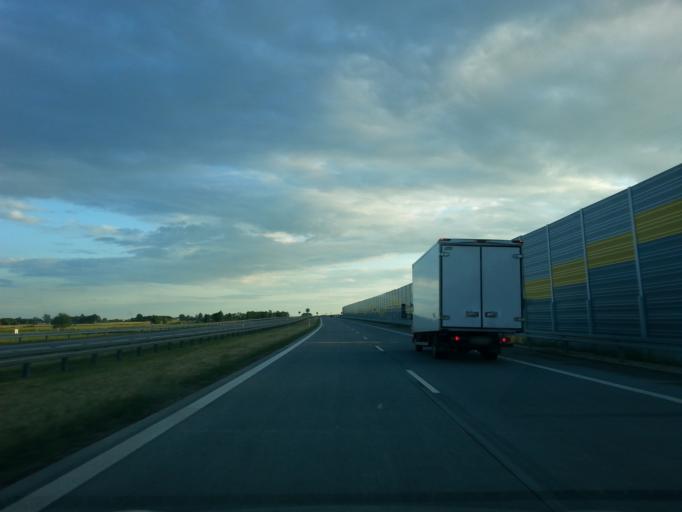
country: PL
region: Lodz Voivodeship
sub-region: Powiat wieruszowski
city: Lututow
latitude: 51.3257
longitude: 18.4404
